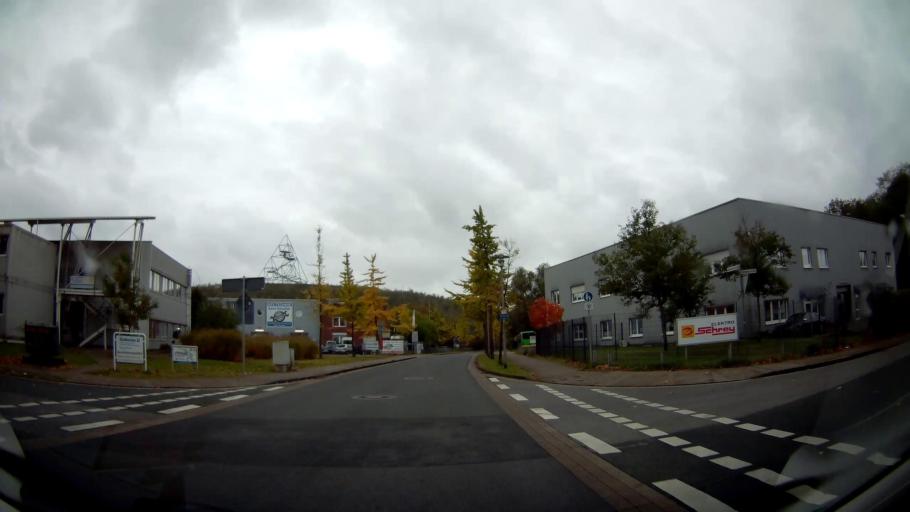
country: DE
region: North Rhine-Westphalia
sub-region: Regierungsbezirk Munster
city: Bottrop
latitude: 51.5321
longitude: 6.9569
